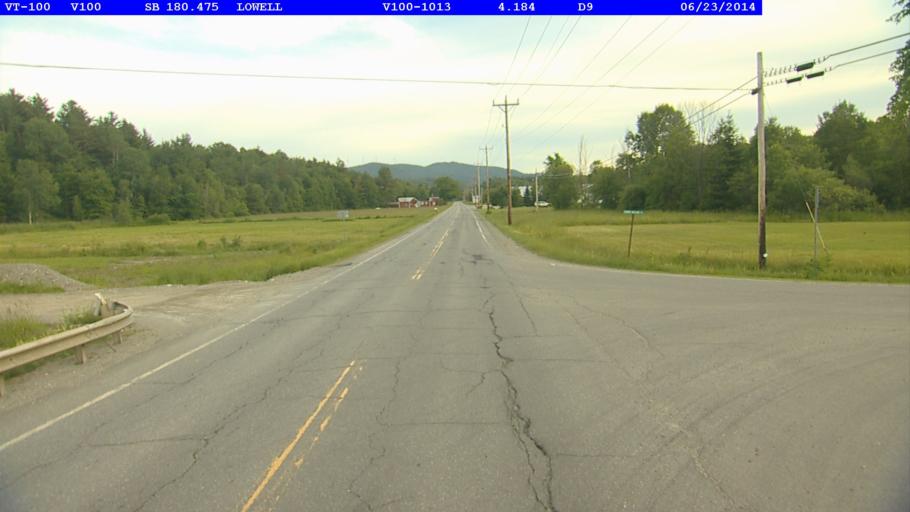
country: US
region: Vermont
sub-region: Lamoille County
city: Hyde Park
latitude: 44.7964
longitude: -72.4479
